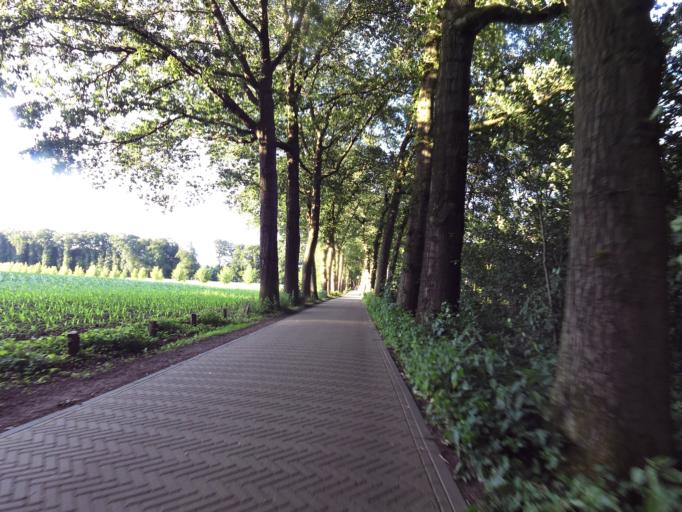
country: NL
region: Gelderland
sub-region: Gemeente Doetinchem
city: Doetinchem
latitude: 51.9755
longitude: 6.2815
